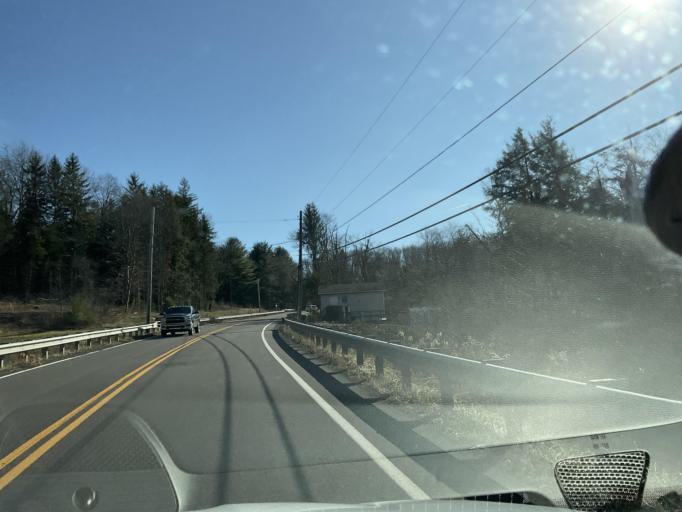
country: US
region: Maryland
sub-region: Garrett County
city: Oakland
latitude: 39.3899
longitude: -79.4607
